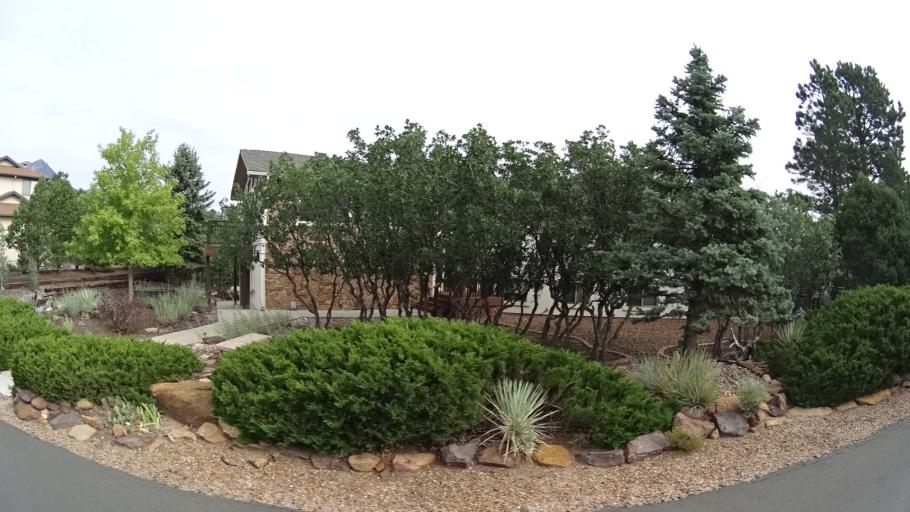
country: US
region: Colorado
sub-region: El Paso County
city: Air Force Academy
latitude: 38.9331
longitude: -104.8557
